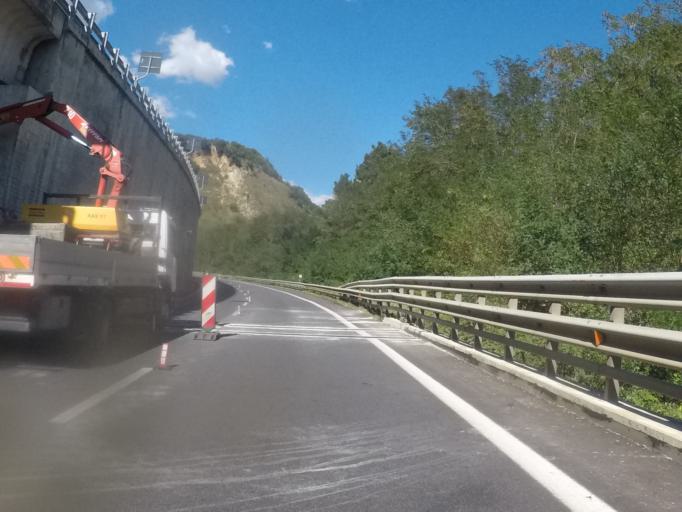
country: IT
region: Calabria
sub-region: Provincia di Cosenza
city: Altilia
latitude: 39.1392
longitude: 16.2745
